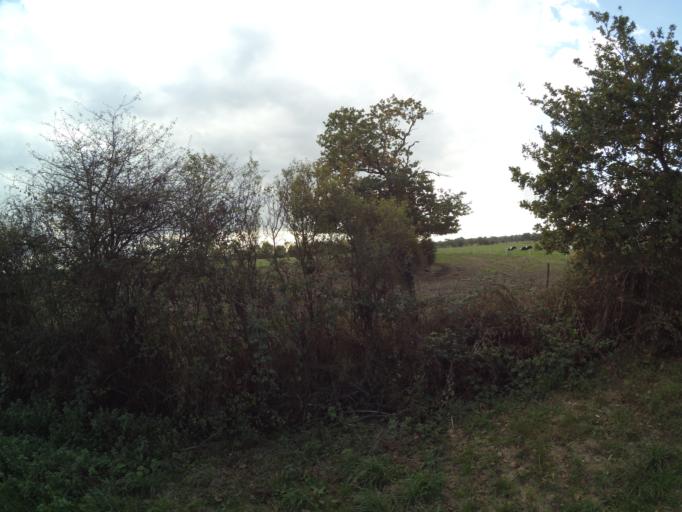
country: FR
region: Pays de la Loire
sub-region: Departement de la Loire-Atlantique
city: Saint-Lumine-de-Clisson
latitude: 47.0730
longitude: -1.3316
